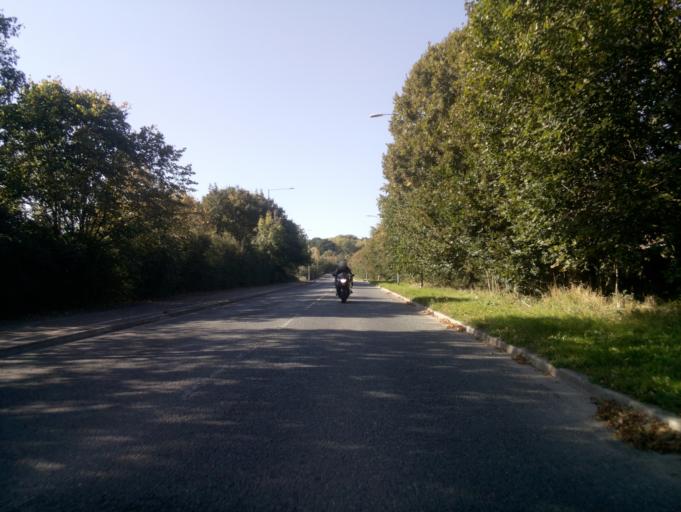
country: GB
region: England
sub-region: West Berkshire
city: Thatcham
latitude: 51.4092
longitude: -1.2464
